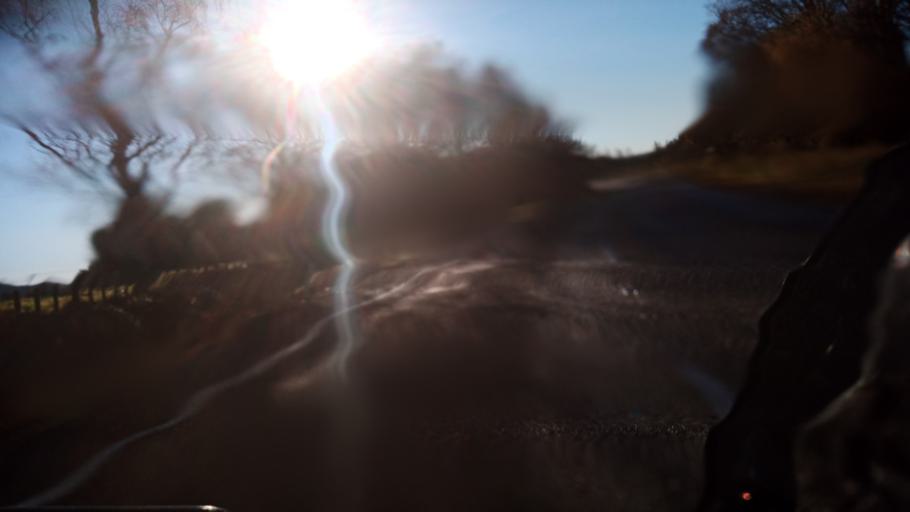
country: NZ
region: Hawke's Bay
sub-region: Wairoa District
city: Wairoa
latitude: -39.0291
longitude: 177.3703
